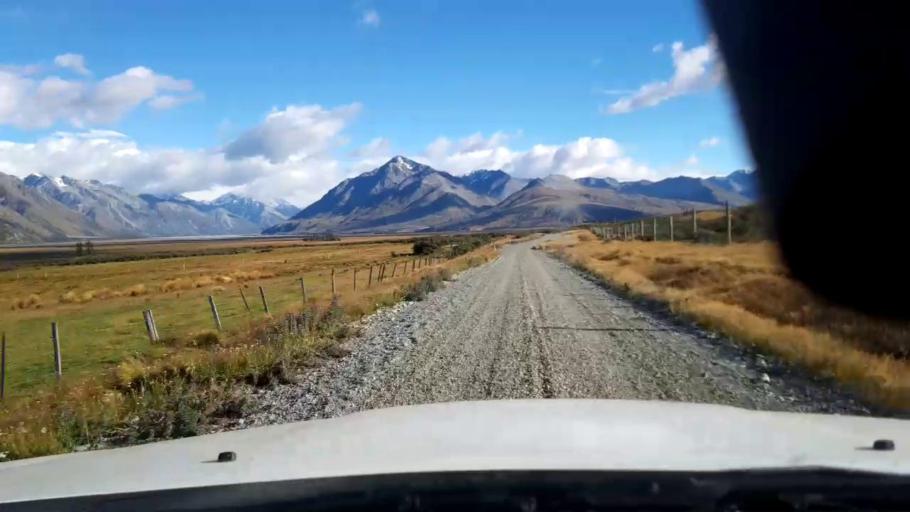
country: NZ
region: Canterbury
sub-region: Timaru District
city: Pleasant Point
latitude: -43.7704
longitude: 170.5691
